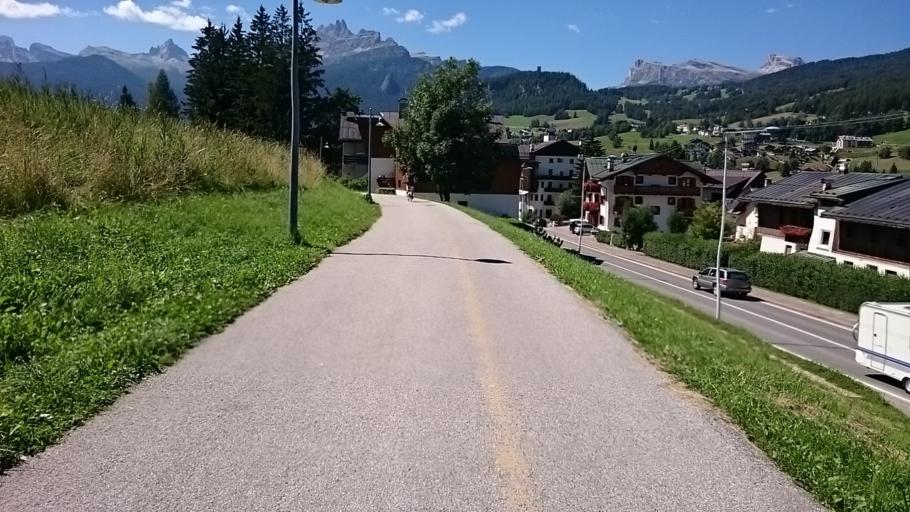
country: IT
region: Veneto
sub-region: Provincia di Belluno
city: Cortina d'Ampezzo
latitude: 46.5434
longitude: 12.1370
